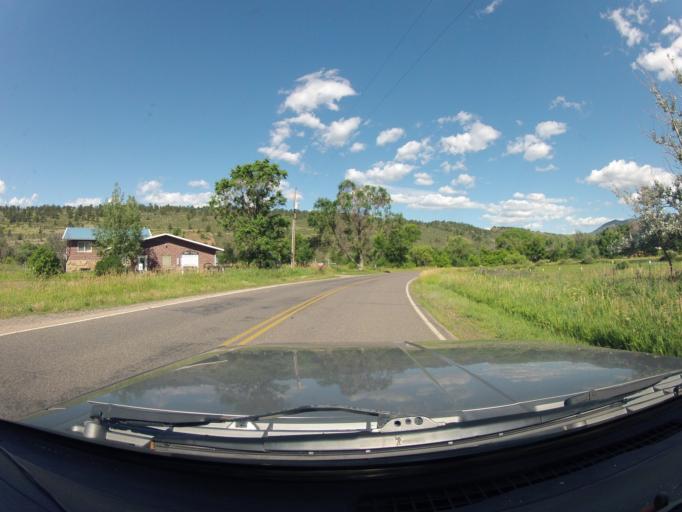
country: US
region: Colorado
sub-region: Larimer County
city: Laporte
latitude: 40.4874
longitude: -105.2144
